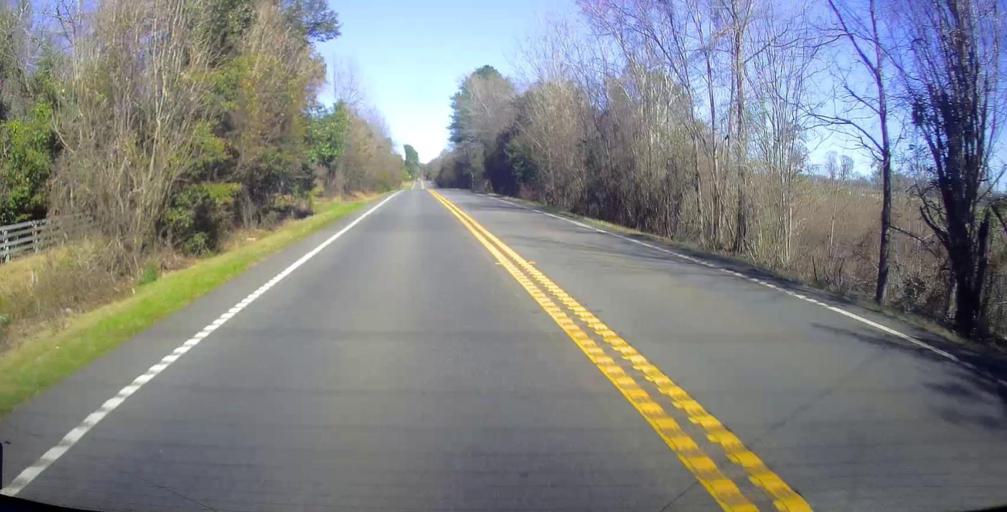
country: US
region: Georgia
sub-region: Macon County
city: Marshallville
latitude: 32.4512
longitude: -83.9661
